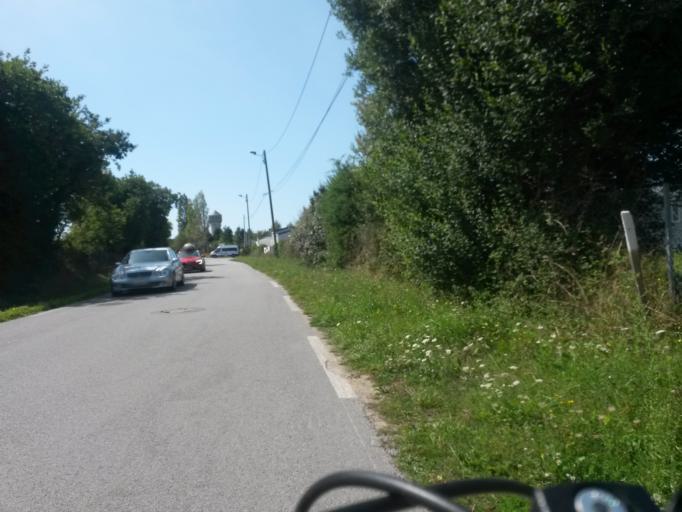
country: FR
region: Pays de la Loire
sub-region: Departement de la Loire-Atlantique
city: Guerande
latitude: 47.3389
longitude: -2.4204
